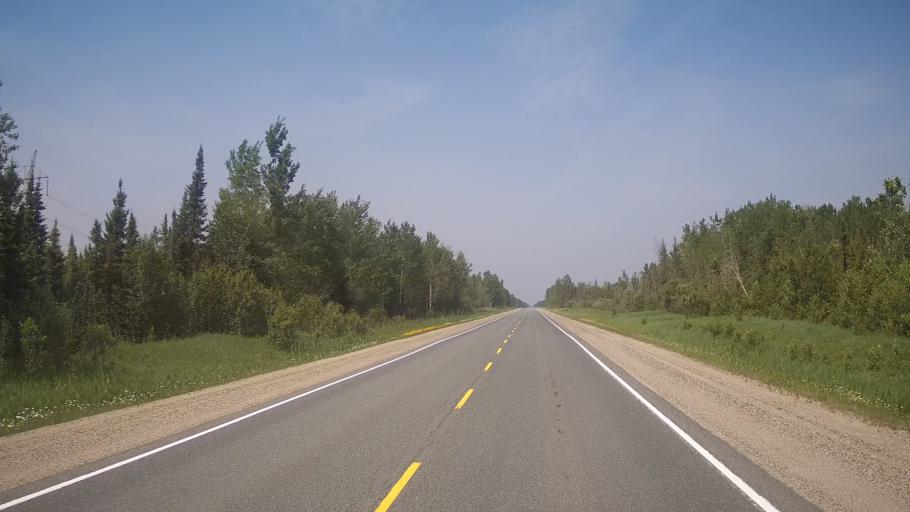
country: CA
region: Ontario
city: Timmins
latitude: 48.8209
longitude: -81.3706
